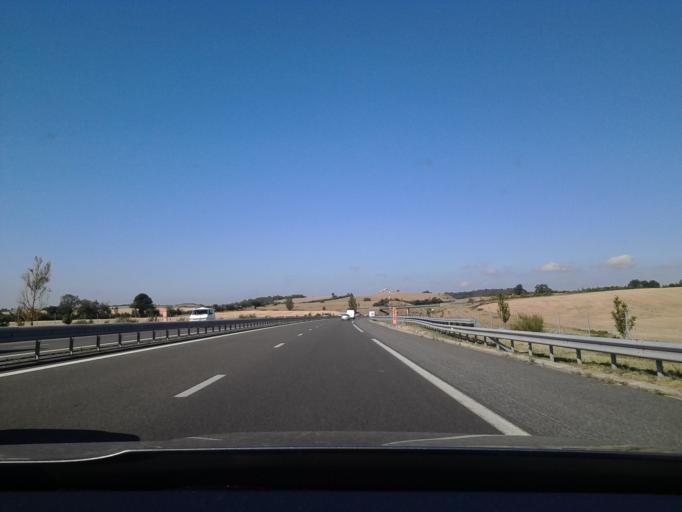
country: FR
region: Midi-Pyrenees
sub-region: Departement de l'Aveyron
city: Severac-le-Chateau
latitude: 44.2658
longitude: 3.0795
